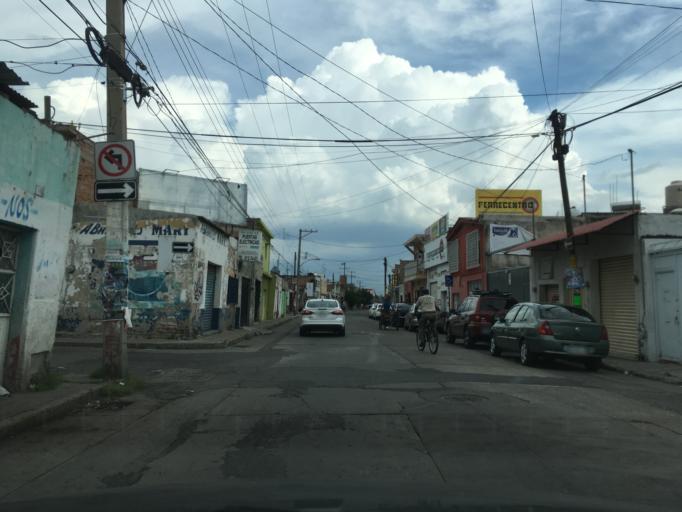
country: MX
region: Guanajuato
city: Celaya
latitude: 20.5171
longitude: -100.8164
